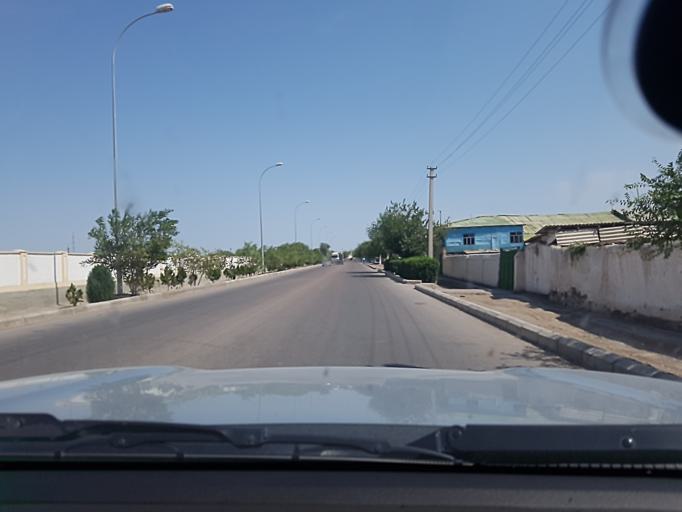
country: TM
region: Dasoguz
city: Koeneuergench
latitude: 42.3243
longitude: 59.1430
